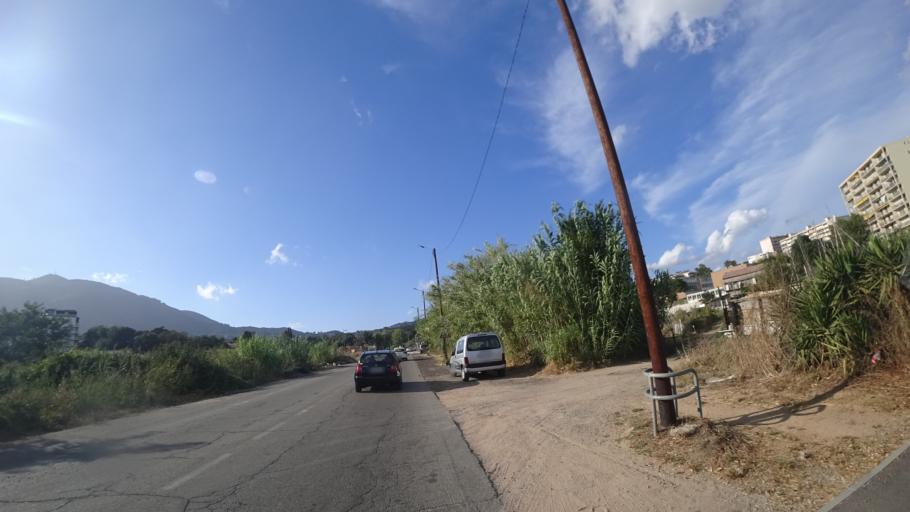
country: FR
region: Corsica
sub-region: Departement de la Corse-du-Sud
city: Ajaccio
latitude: 41.9377
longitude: 8.7424
